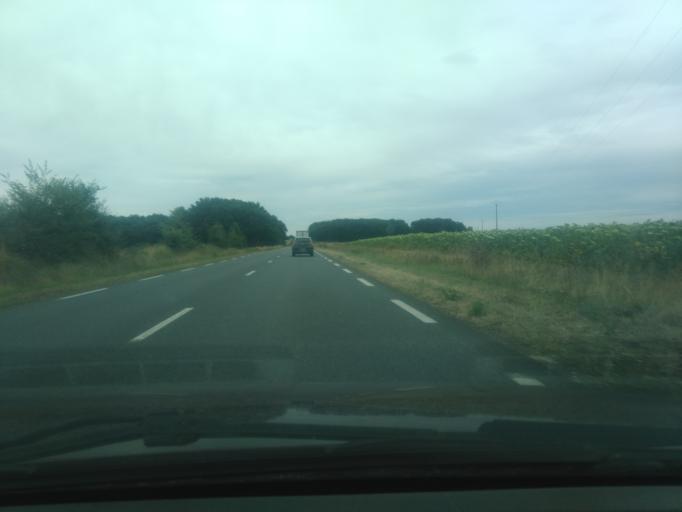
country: FR
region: Poitou-Charentes
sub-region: Departement de la Vienne
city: Saint-Savin
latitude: 46.5738
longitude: 0.8013
